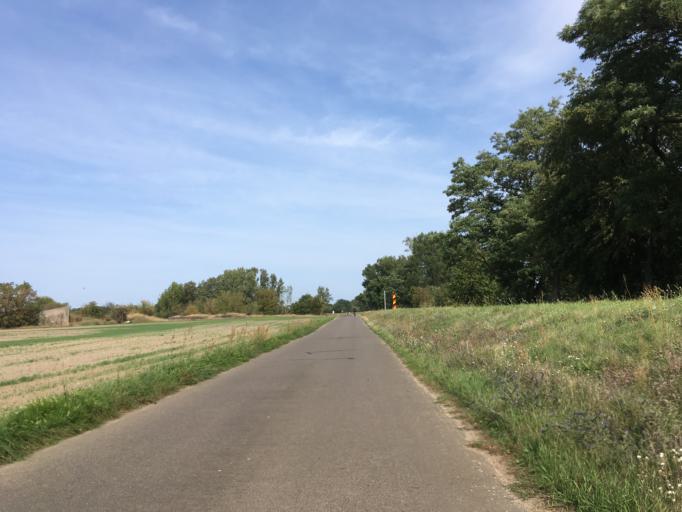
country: DE
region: Brandenburg
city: Guben
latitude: 51.9902
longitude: 14.7170
